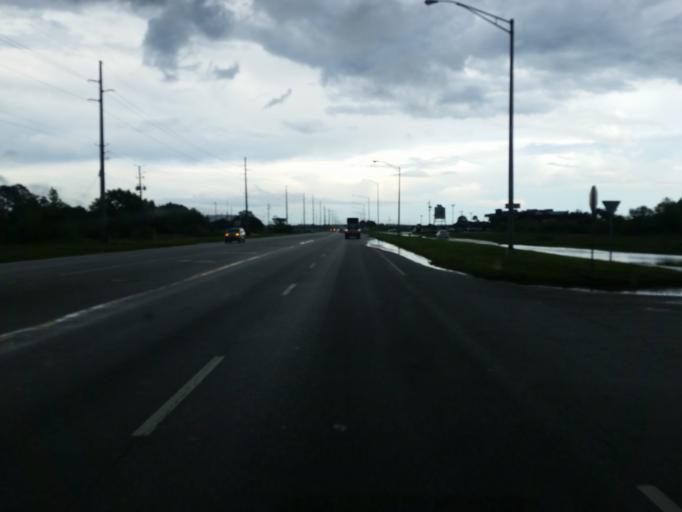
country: US
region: Alabama
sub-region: Mobile County
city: Mobile
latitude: 30.6803
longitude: -88.0007
